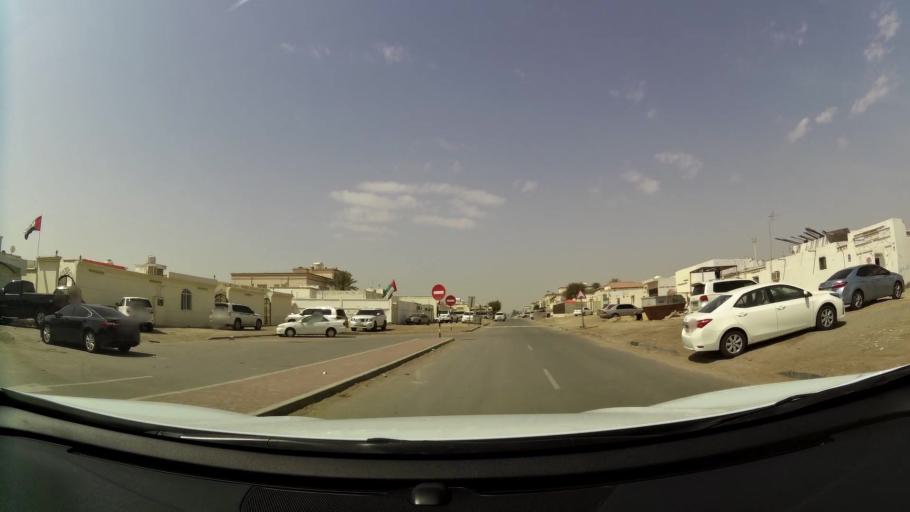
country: AE
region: Abu Dhabi
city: Abu Dhabi
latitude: 24.2947
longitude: 54.6496
